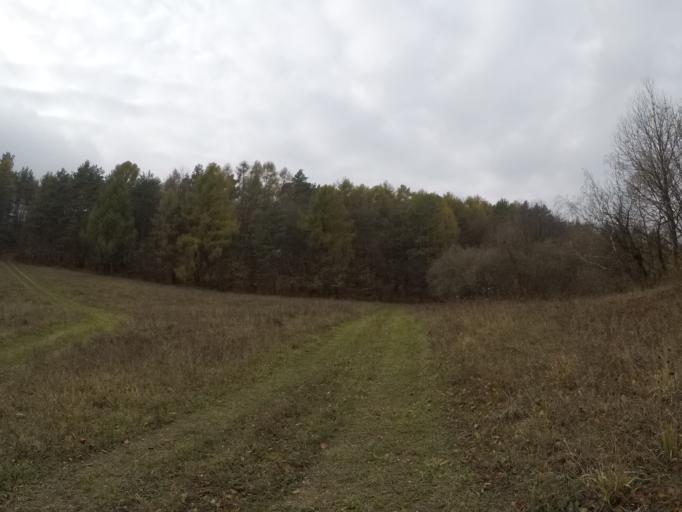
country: SK
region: Presovsky
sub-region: Okres Presov
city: Presov
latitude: 48.9025
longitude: 21.1712
